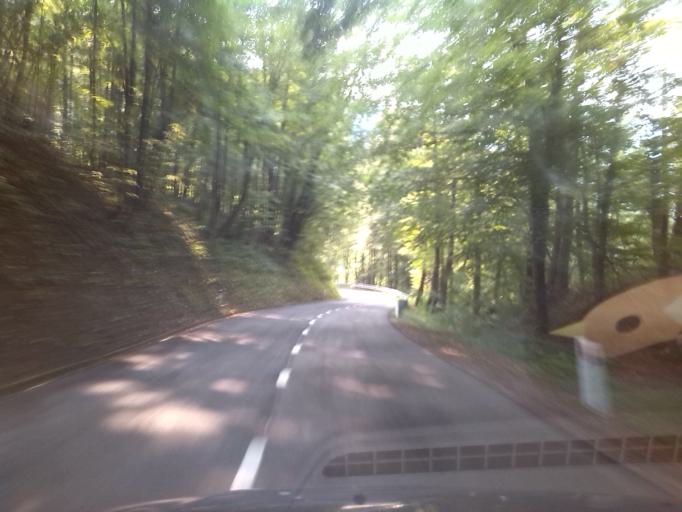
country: SI
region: Kobarid
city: Kobarid
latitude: 46.2191
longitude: 13.5930
